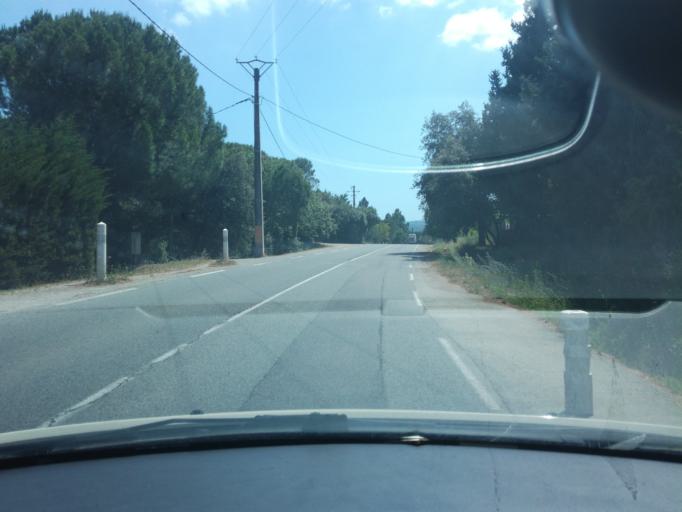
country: FR
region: Provence-Alpes-Cote d'Azur
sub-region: Departement du Var
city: Le Muy
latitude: 43.4858
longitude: 6.5674
